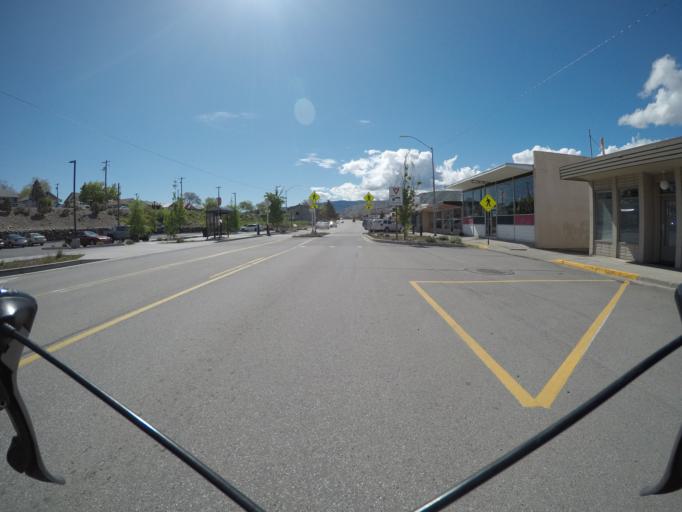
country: US
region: Washington
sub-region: Douglas County
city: East Wenatchee
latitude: 47.4149
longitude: -120.2930
